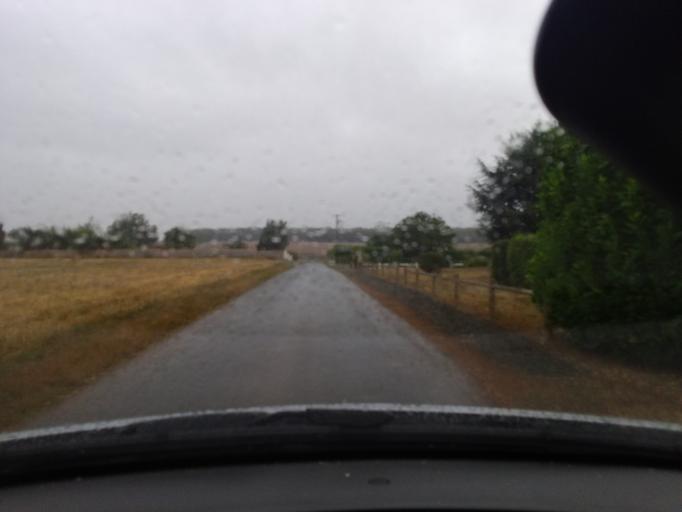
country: FR
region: Pays de la Loire
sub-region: Departement de la Vendee
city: Sainte-Gemme-la-Plaine
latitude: 46.4867
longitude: -1.1222
